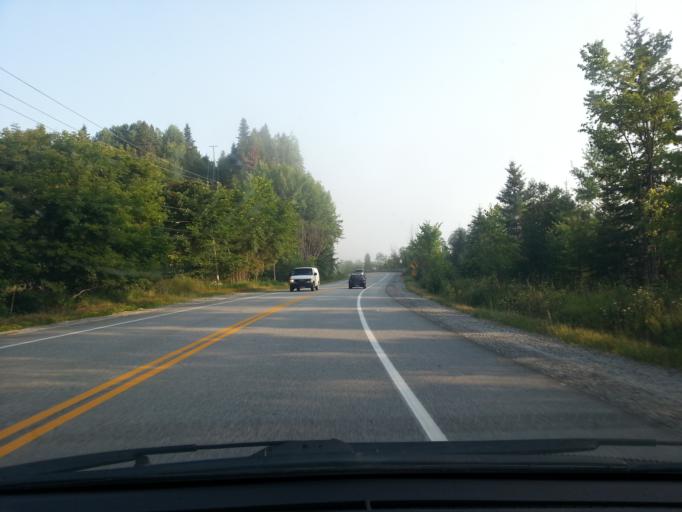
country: CA
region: Quebec
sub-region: Outaouais
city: Wakefield
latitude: 45.6893
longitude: -75.9317
